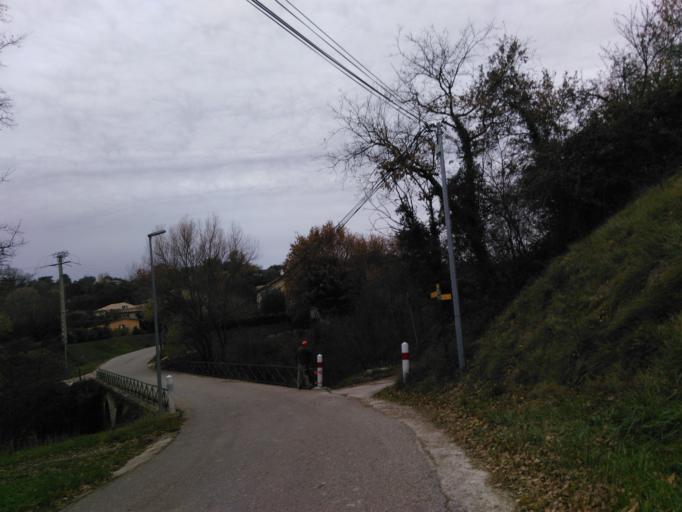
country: FR
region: Provence-Alpes-Cote d'Azur
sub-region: Departement du Vaucluse
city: Vaison-la-Romaine
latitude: 44.2605
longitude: 5.1101
